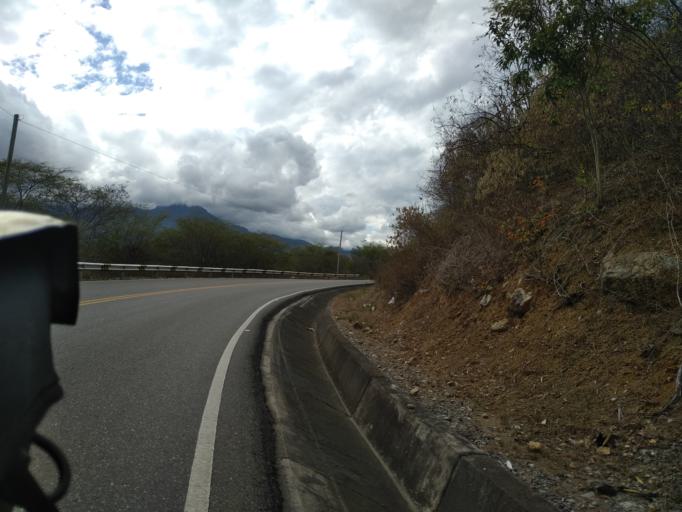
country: PE
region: Amazonas
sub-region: Utcubamba
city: Jamalca
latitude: -5.8244
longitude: -78.2578
